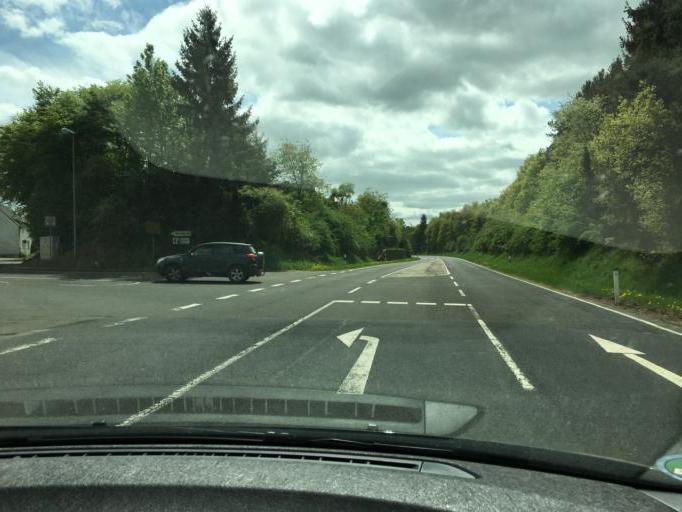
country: DE
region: Rheinland-Pfalz
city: Kirchsahr
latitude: 50.5198
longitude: 6.8609
